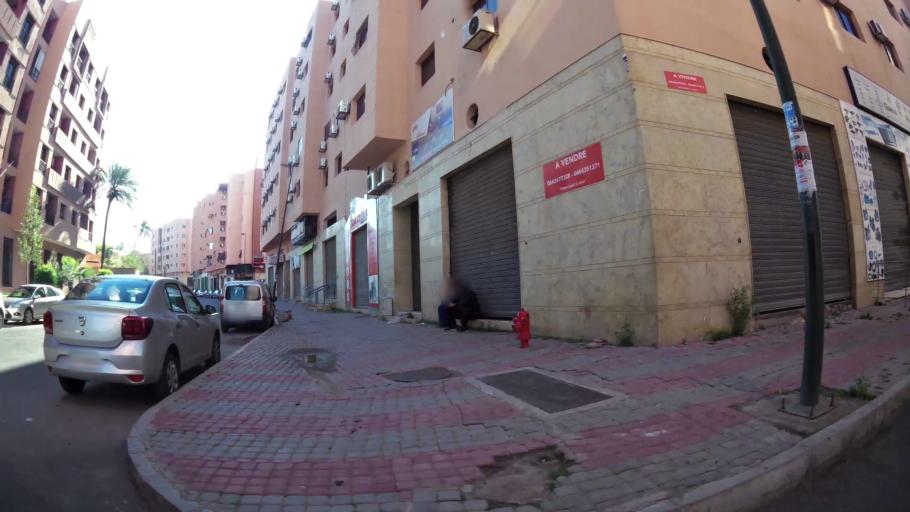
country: MA
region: Marrakech-Tensift-Al Haouz
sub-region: Marrakech
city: Marrakesh
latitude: 31.6518
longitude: -8.0192
